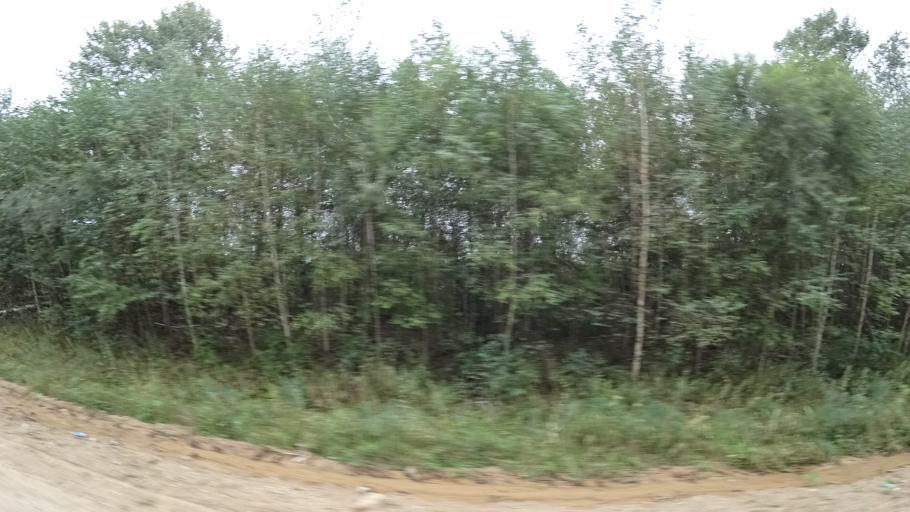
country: RU
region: Primorskiy
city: Rettikhovka
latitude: 44.1479
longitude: 132.6767
